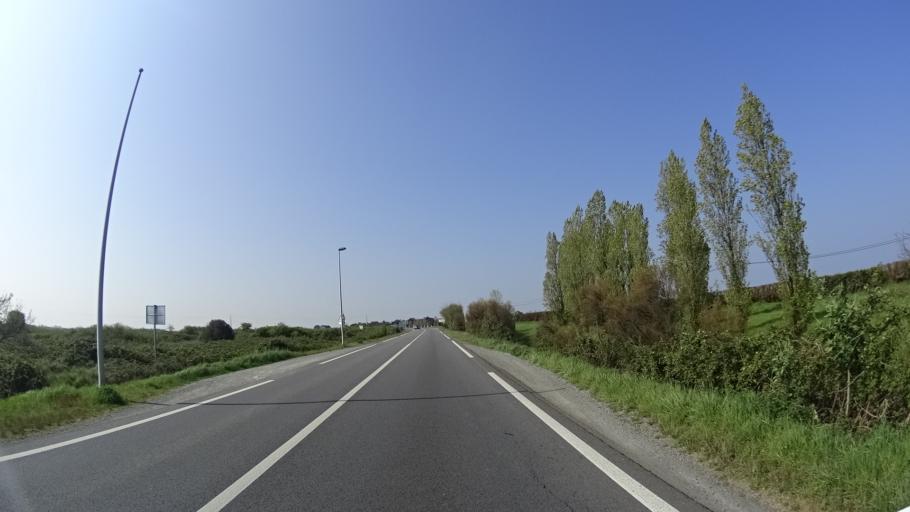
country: FR
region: Pays de la Loire
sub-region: Departement de la Loire-Atlantique
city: Bourgneuf-en-Retz
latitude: 47.0392
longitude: -1.9584
